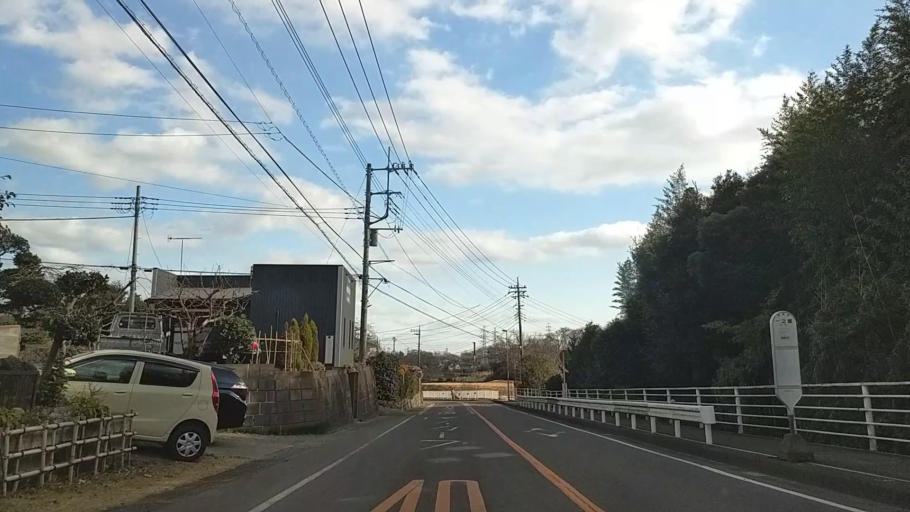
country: JP
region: Kanagawa
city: Isehara
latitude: 35.4204
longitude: 139.2913
